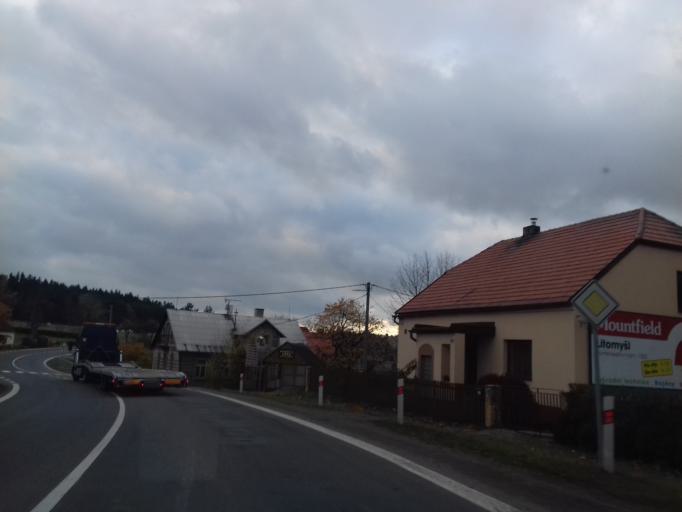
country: CZ
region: Pardubicky
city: Pomezi
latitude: 49.7340
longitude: 16.3512
